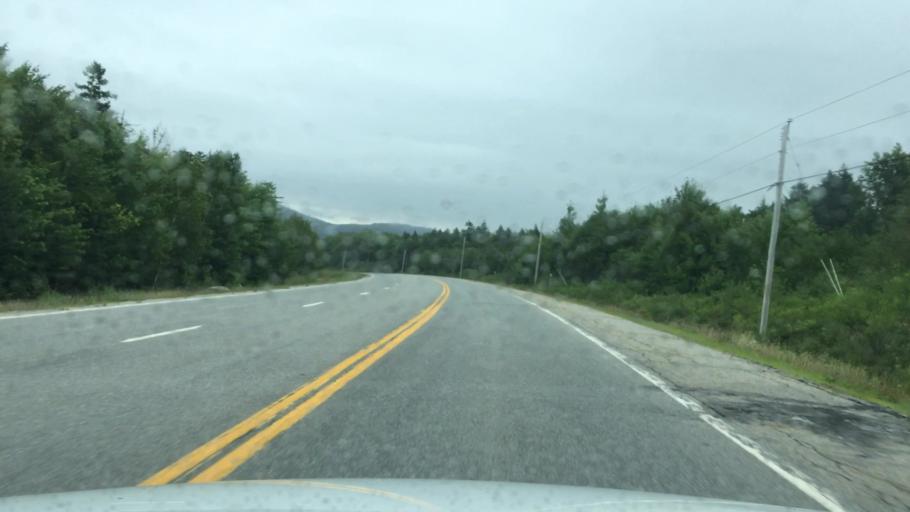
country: US
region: Maine
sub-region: Hancock County
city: Franklin
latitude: 44.8247
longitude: -68.1071
